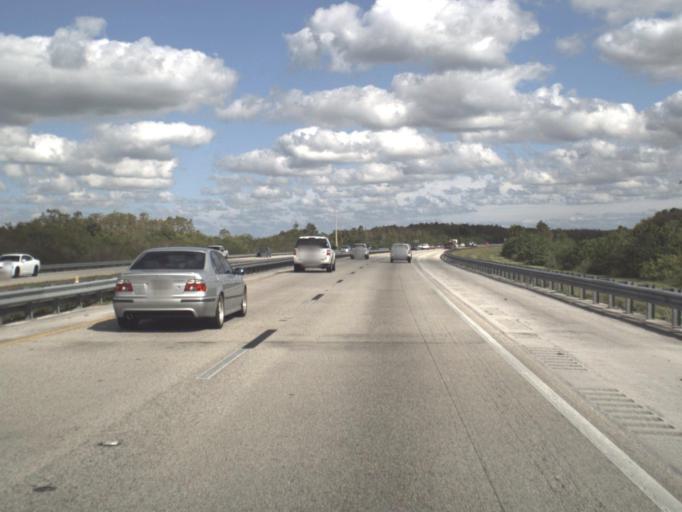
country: US
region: Florida
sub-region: Indian River County
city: West Vero Corridor
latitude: 27.5593
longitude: -80.6528
